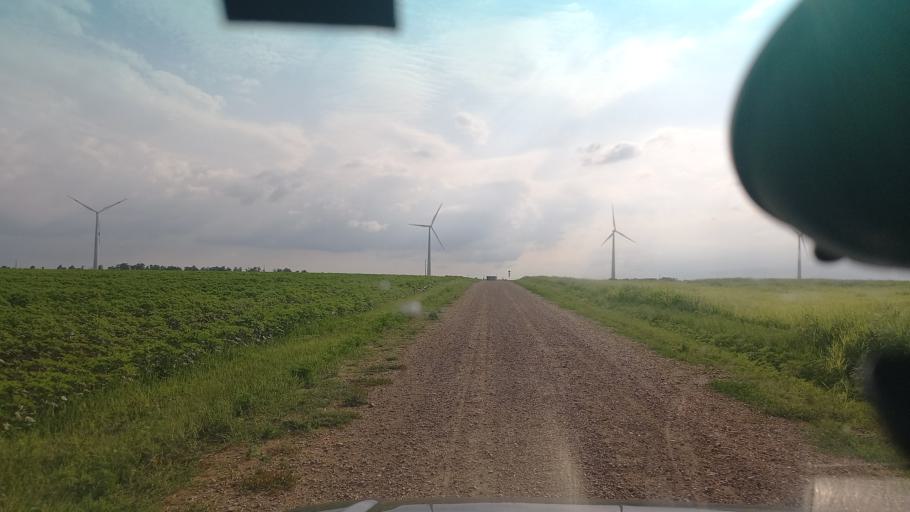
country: RU
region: Adygeya
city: Giaginskaya
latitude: 44.9528
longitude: 40.0882
